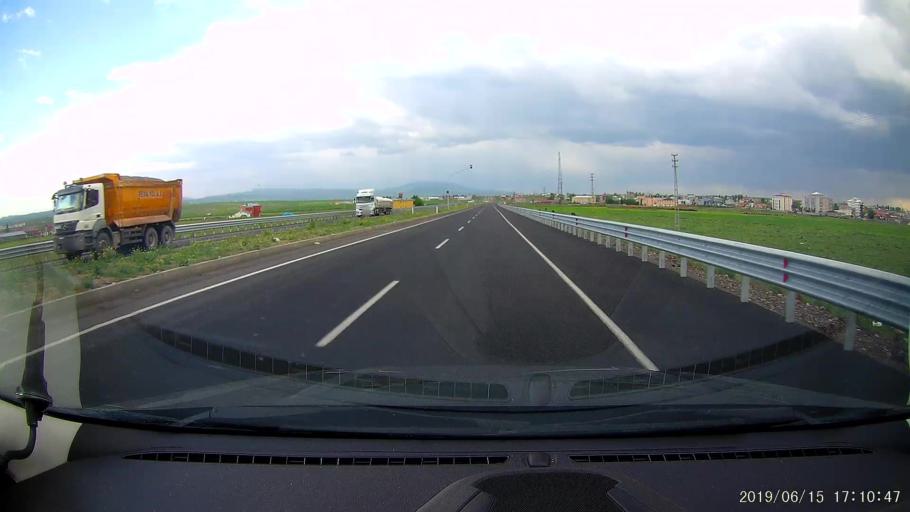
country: TR
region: Kars
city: Kars
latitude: 40.6183
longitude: 43.1335
